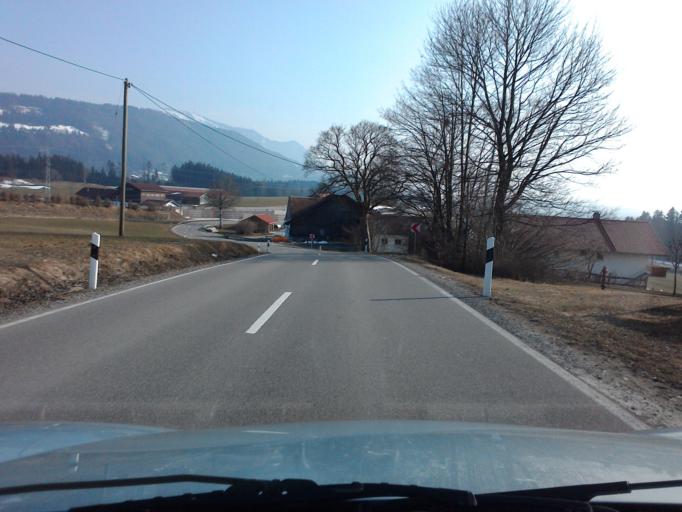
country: DE
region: Bavaria
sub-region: Swabia
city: Rettenberg
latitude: 47.6167
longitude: 10.2737
